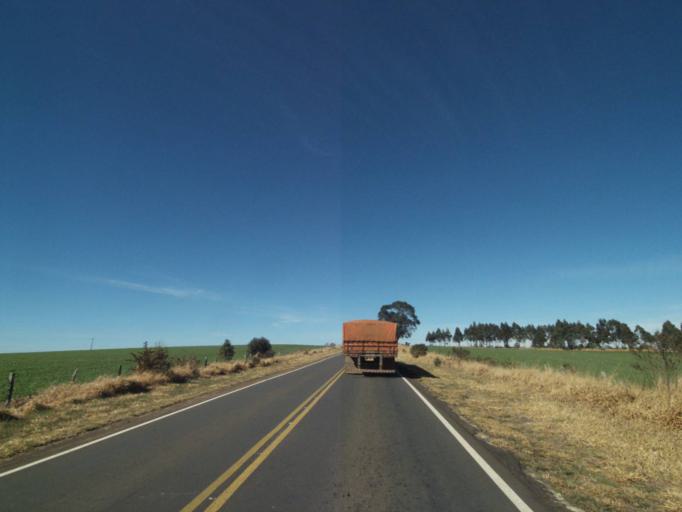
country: BR
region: Parana
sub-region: Tibagi
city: Tibagi
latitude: -24.6231
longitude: -50.2494
